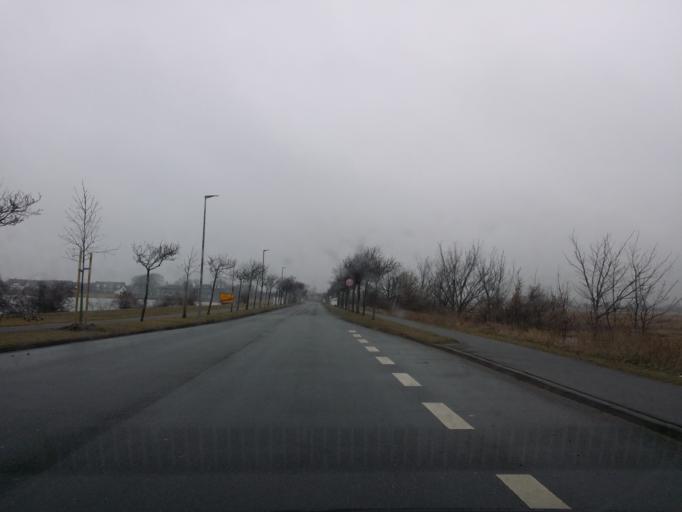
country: DE
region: Schleswig-Holstein
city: Burg auf Fehmarn
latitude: 54.4145
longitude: 11.2116
